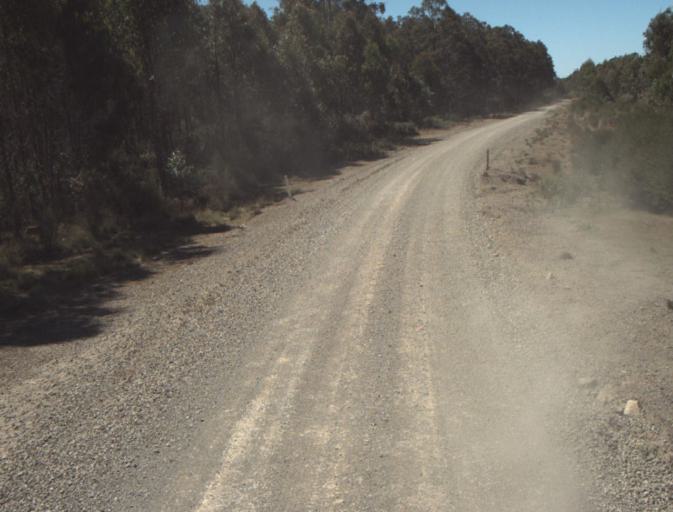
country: AU
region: Tasmania
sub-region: Dorset
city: Scottsdale
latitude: -41.3047
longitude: 147.4674
